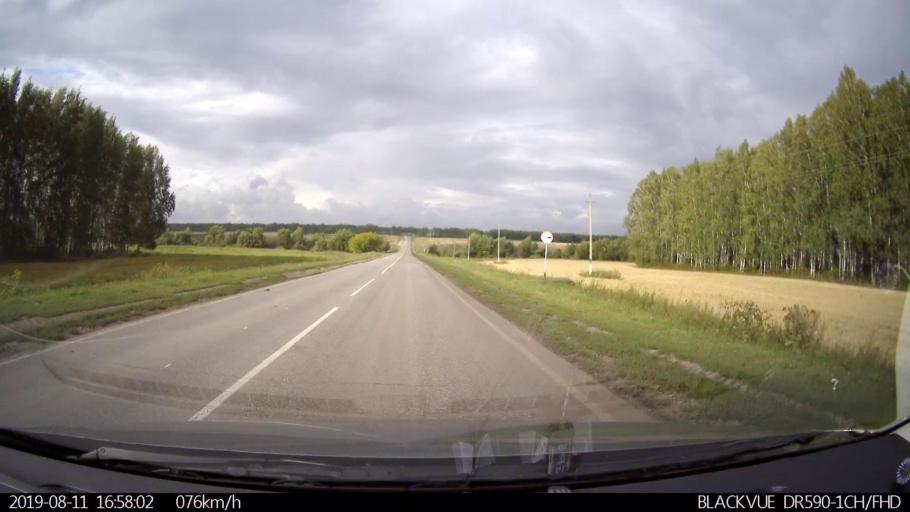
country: RU
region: Ulyanovsk
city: Mayna
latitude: 54.3044
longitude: 47.6551
